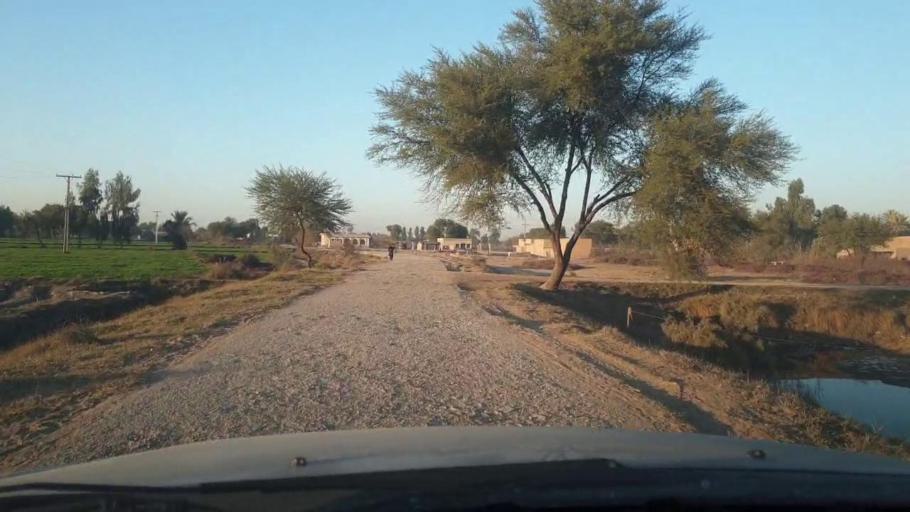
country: PK
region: Sindh
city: Pano Aqil
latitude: 27.9050
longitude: 69.1976
